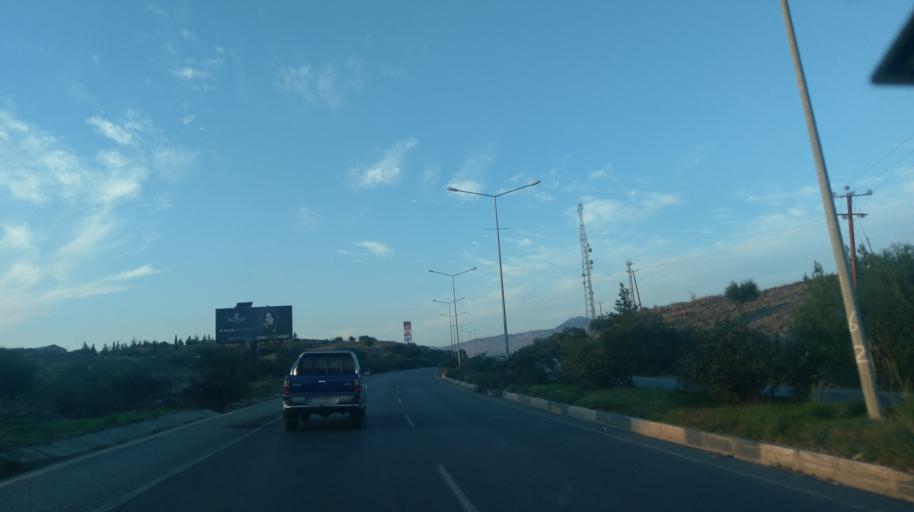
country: CY
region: Lefkosia
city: Nicosia
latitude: 35.2285
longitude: 33.3125
